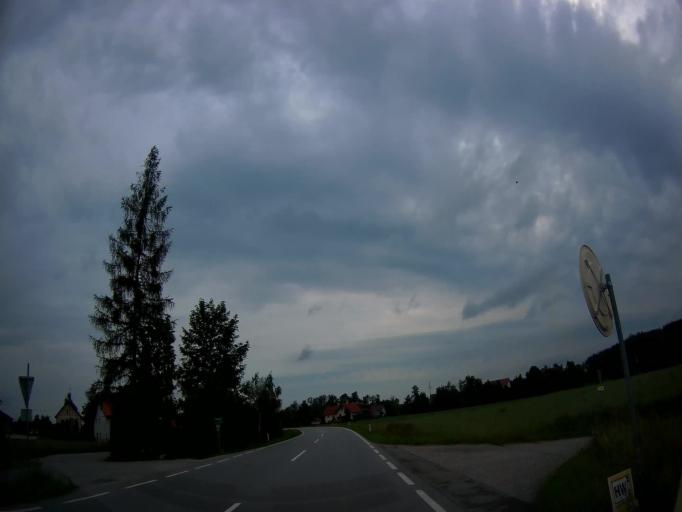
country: AT
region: Upper Austria
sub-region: Politischer Bezirk Braunau am Inn
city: Altheim
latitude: 48.2245
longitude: 13.1703
